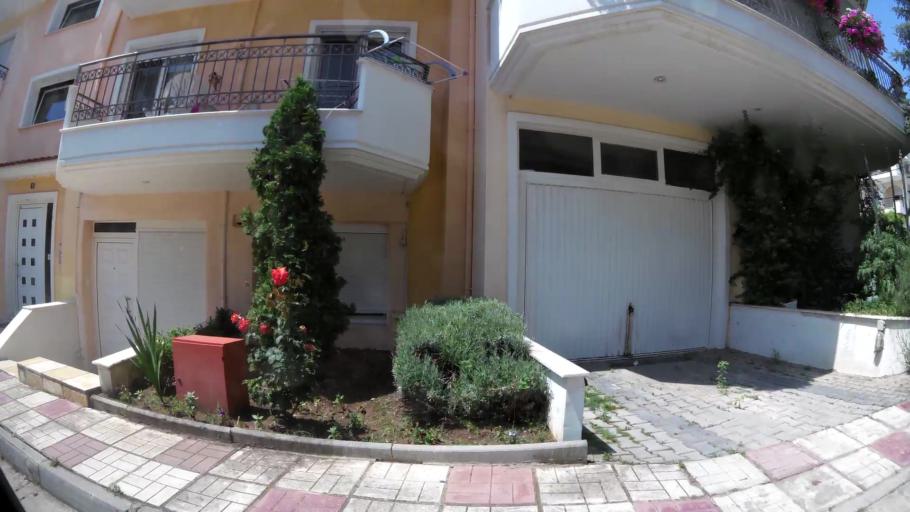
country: GR
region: West Macedonia
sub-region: Nomos Kozanis
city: Kozani
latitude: 40.3013
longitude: 21.7787
